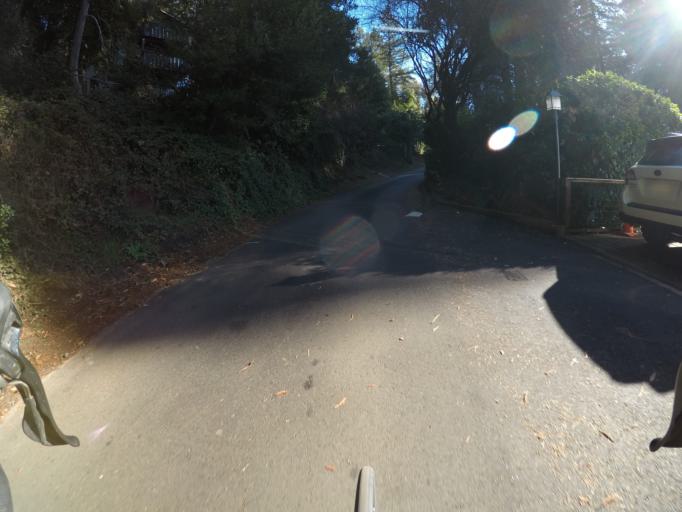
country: US
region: California
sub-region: Santa Cruz County
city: Mount Hermon
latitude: 37.0479
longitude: -122.0624
